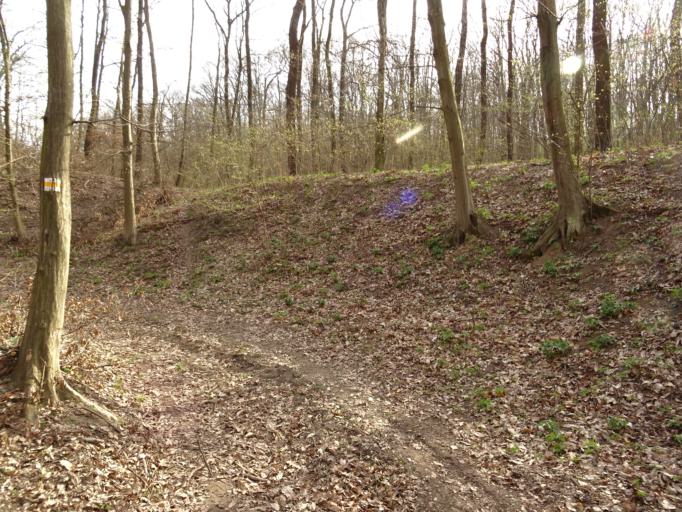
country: HU
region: Fejer
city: Lovasbereny
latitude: 47.2726
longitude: 18.5960
